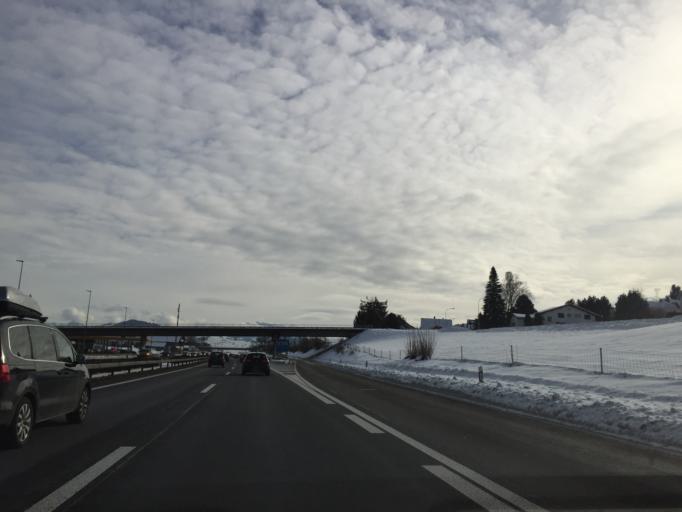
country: CH
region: Zurich
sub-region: Bezirk Horgen
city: Waedenswil / Untermosen-Fuhr
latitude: 47.2219
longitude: 8.6585
